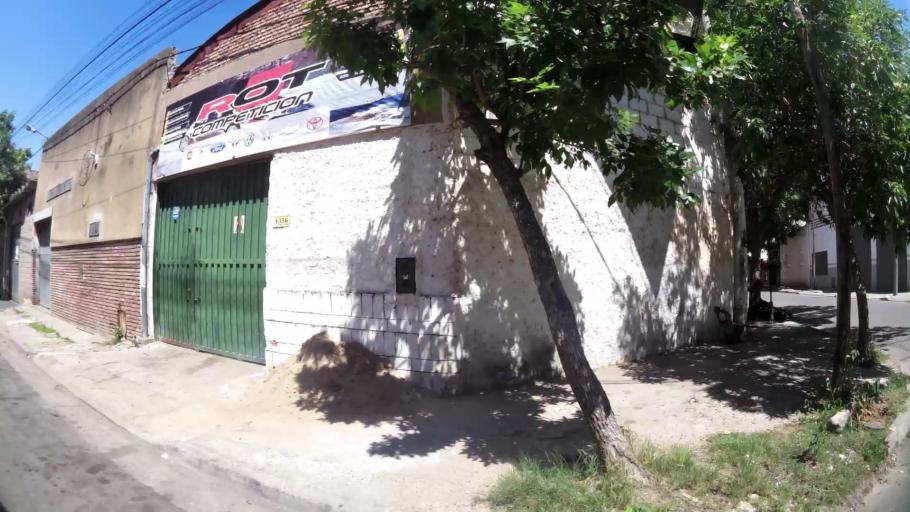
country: AR
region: Cordoba
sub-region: Departamento de Capital
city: Cordoba
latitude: -31.4282
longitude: -64.2021
